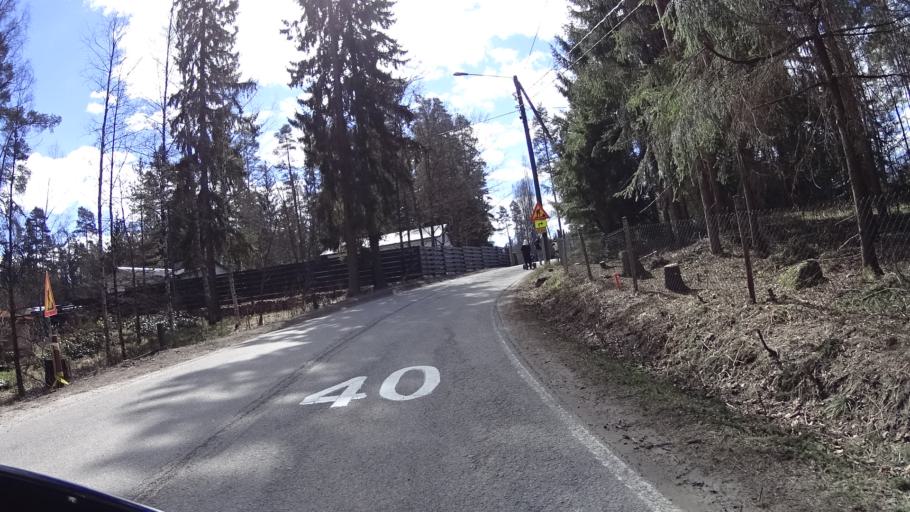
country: FI
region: Uusimaa
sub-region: Helsinki
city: Espoo
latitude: 60.2693
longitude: 24.5294
